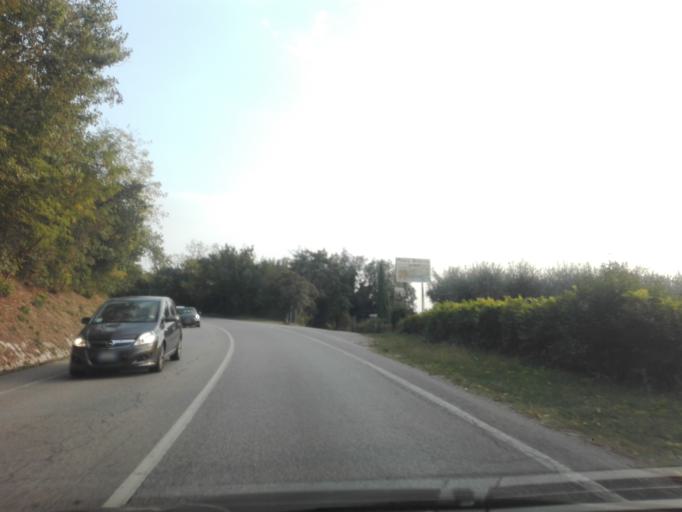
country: IT
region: Veneto
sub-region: Provincia di Verona
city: Lazise
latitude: 45.4932
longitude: 10.7564
